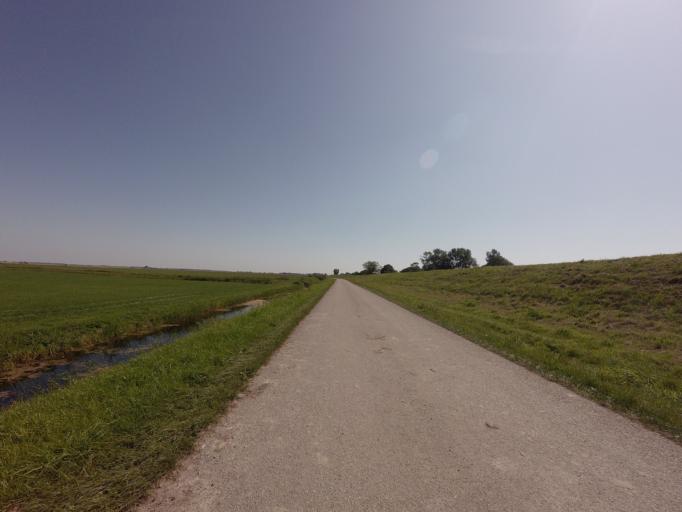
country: NL
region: Friesland
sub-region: Gemeente Dongeradeel
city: Anjum
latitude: 53.3936
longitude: 6.1138
